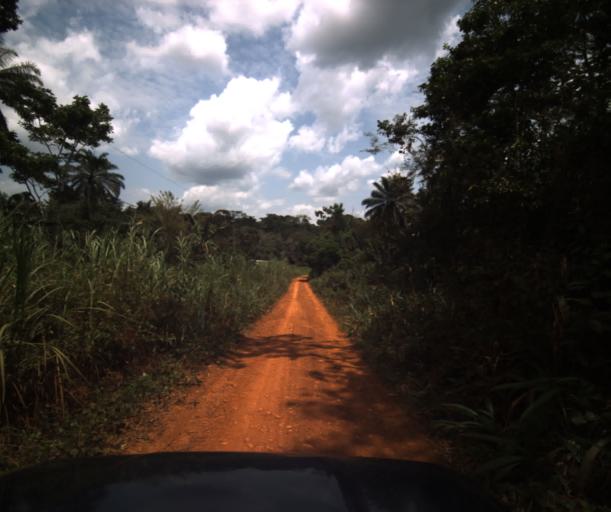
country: CM
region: Centre
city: Eseka
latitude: 3.5485
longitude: 10.9265
